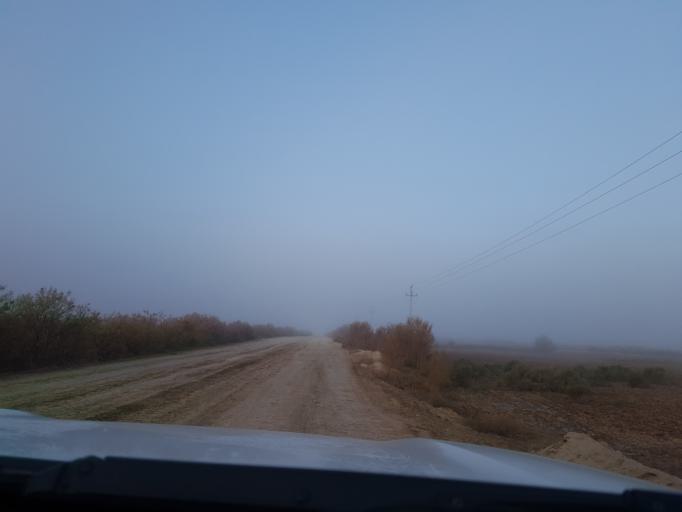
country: TM
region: Dasoguz
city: Koeneuergench
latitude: 41.8451
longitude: 58.4675
